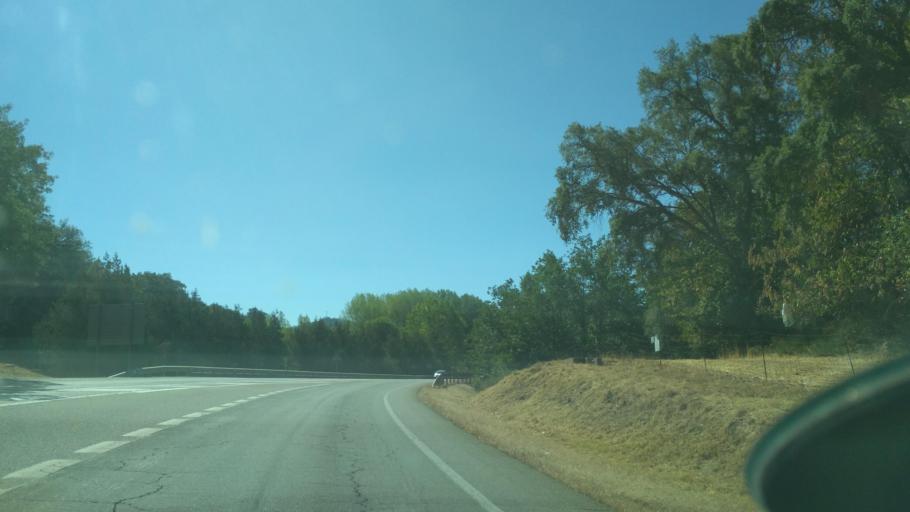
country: ES
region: Andalusia
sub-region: Provincia de Huelva
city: Galaroza
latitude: 37.9208
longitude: -6.6886
